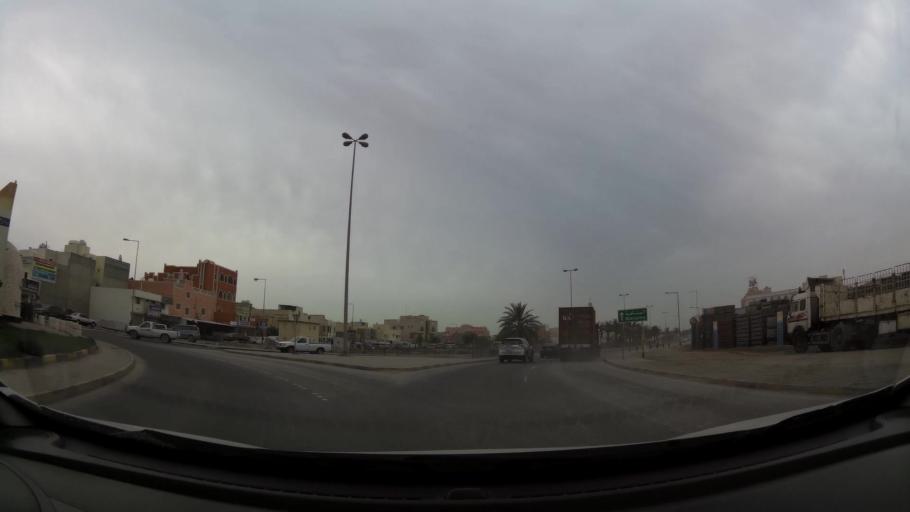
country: BH
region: Northern
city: Madinat `Isa
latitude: 26.1858
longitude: 50.5264
